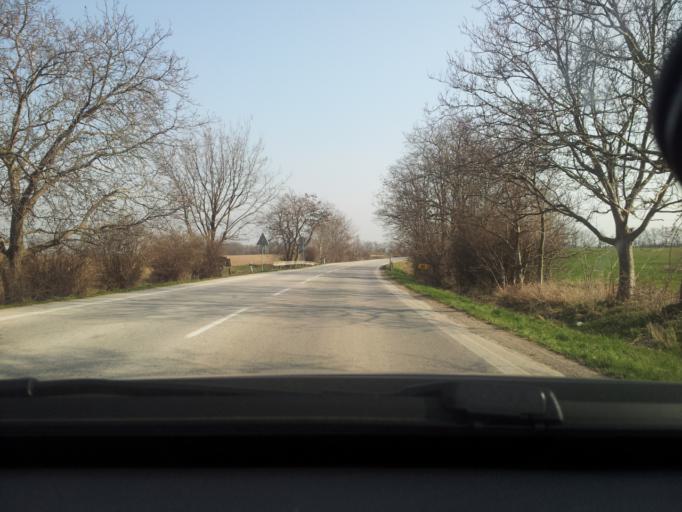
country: SK
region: Trnavsky
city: Leopoldov
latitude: 48.4397
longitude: 17.7021
